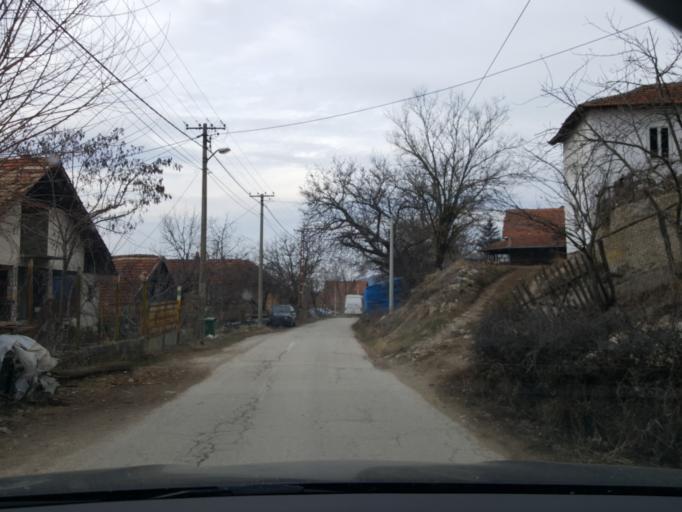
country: RS
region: Central Serbia
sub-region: Pirotski Okrug
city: Dimitrovgrad
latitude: 43.0032
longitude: 22.7628
